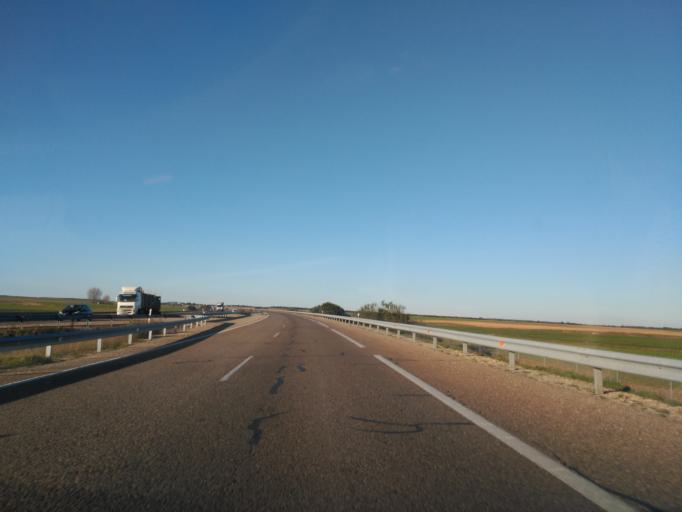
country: ES
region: Castille and Leon
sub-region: Provincia de Salamanca
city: Pajares de la Laguna
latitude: 41.1107
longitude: -5.4903
